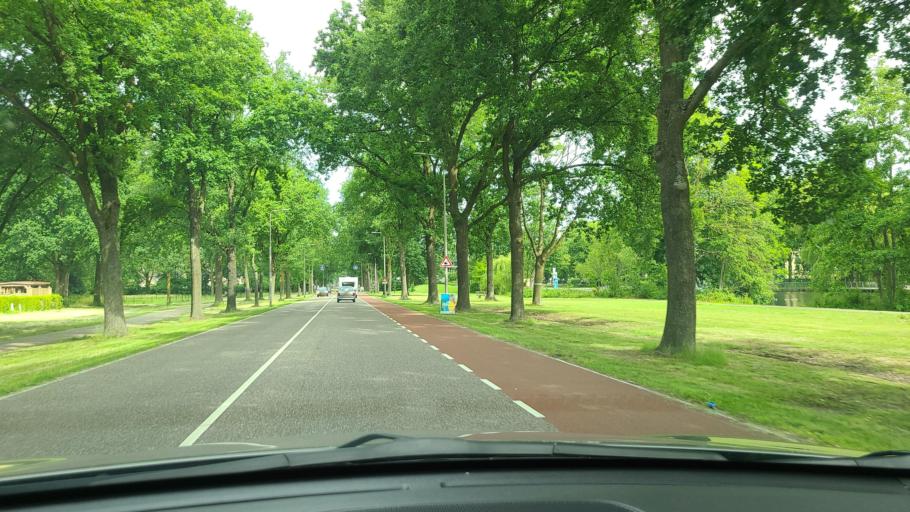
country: NL
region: North Brabant
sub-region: Gemeente Oss
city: Oss
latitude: 51.7491
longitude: 5.5022
